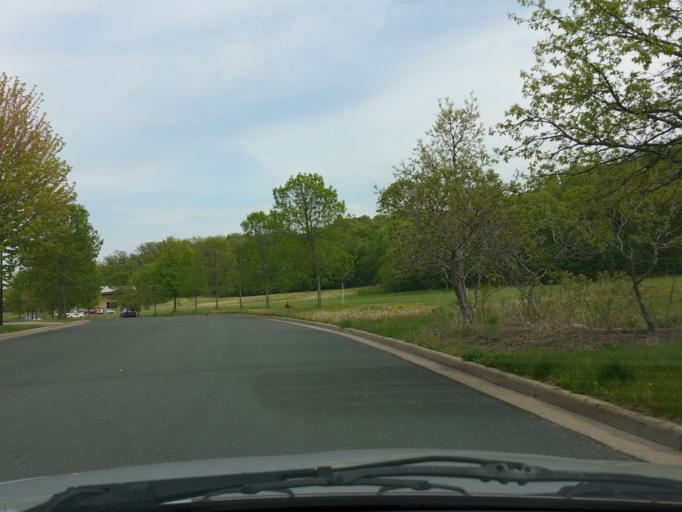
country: US
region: Wisconsin
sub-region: Pierce County
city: River Falls
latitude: 44.8846
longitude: -92.6325
